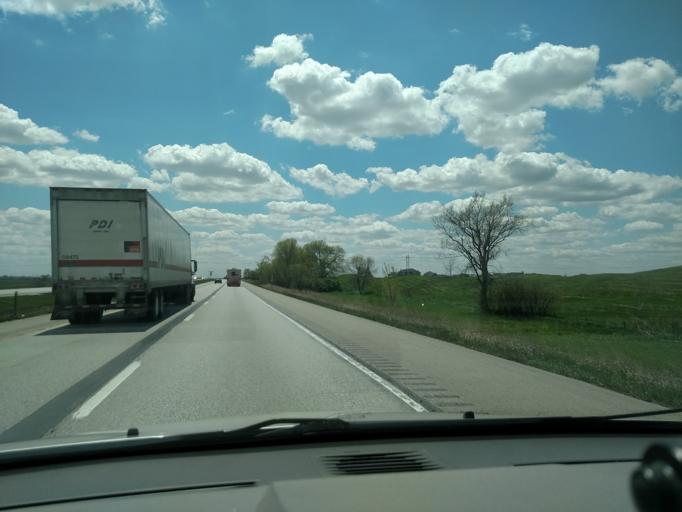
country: US
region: Iowa
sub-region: Polk County
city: Ankeny
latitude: 41.7757
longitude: -93.5709
